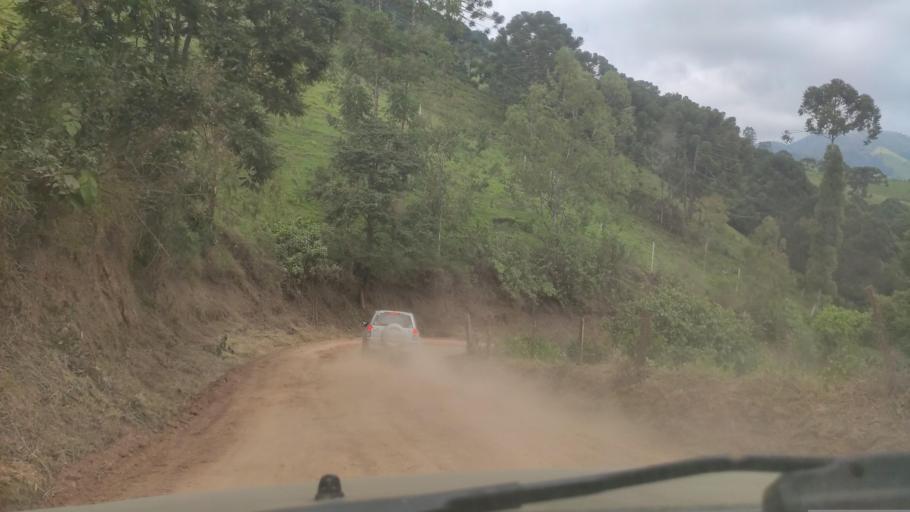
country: BR
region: Minas Gerais
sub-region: Cambui
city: Cambui
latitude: -22.6608
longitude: -45.9138
